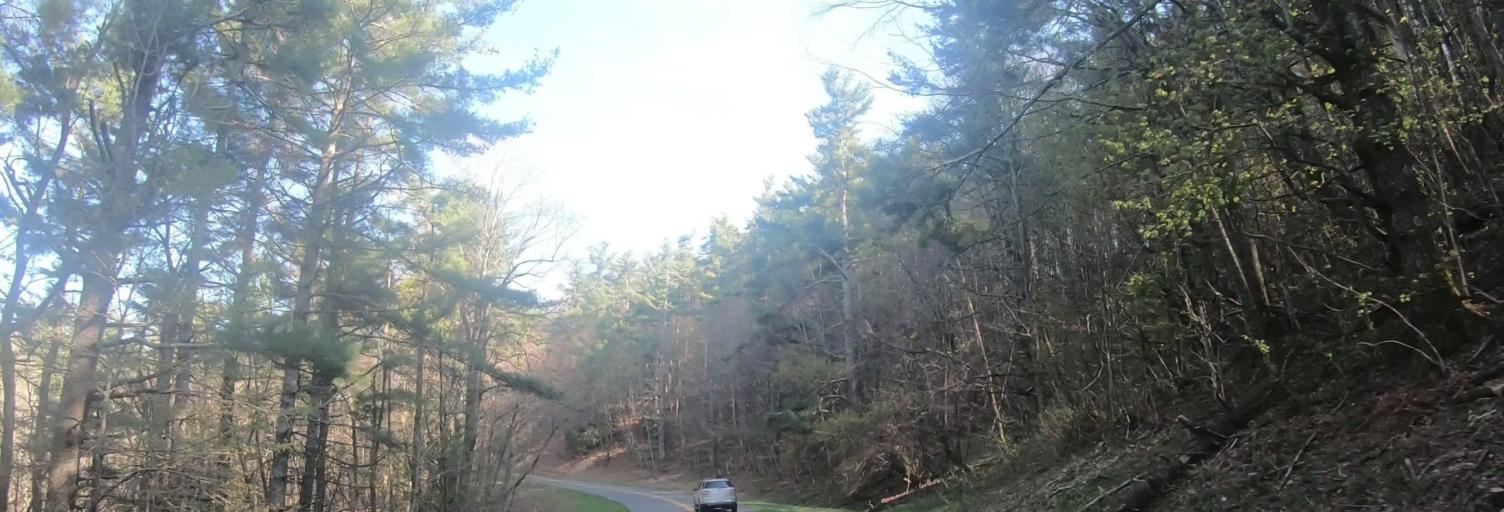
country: US
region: North Carolina
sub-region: Ashe County
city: West Jefferson
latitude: 36.2358
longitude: -81.4931
